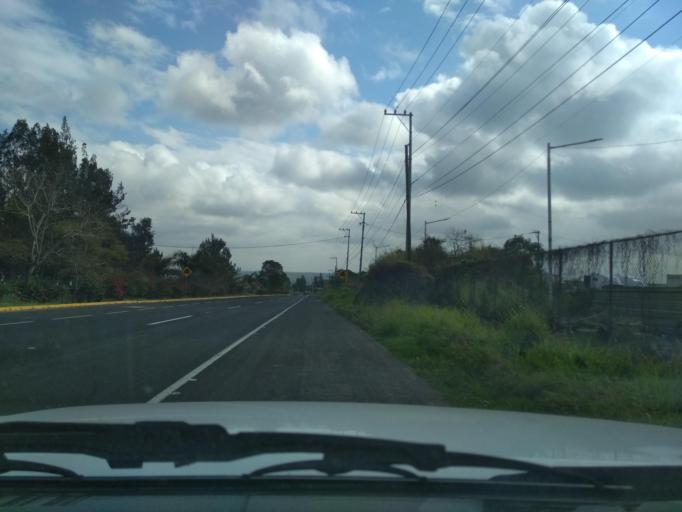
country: MX
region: Veracruz
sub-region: Emiliano Zapata
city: Jacarandas
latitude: 19.4993
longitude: -96.8367
